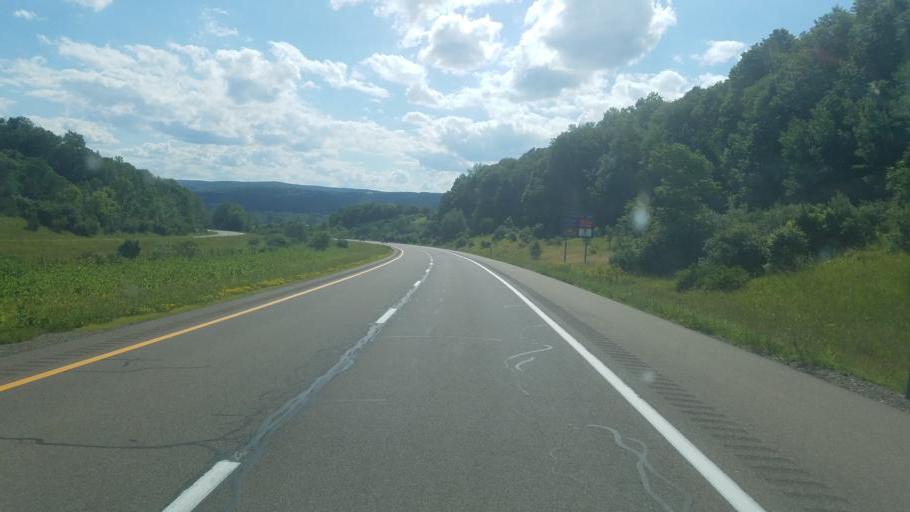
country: US
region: New York
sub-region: Steuben County
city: Hornell
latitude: 42.3802
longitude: -77.6627
